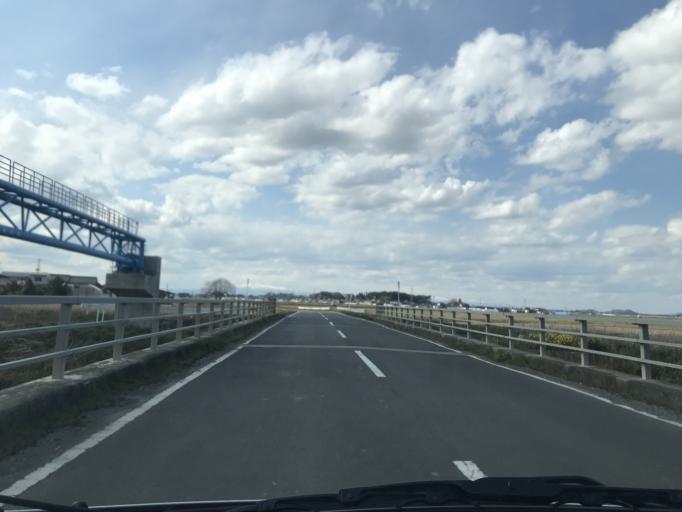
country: JP
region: Miyagi
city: Wakuya
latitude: 38.6576
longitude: 141.2331
